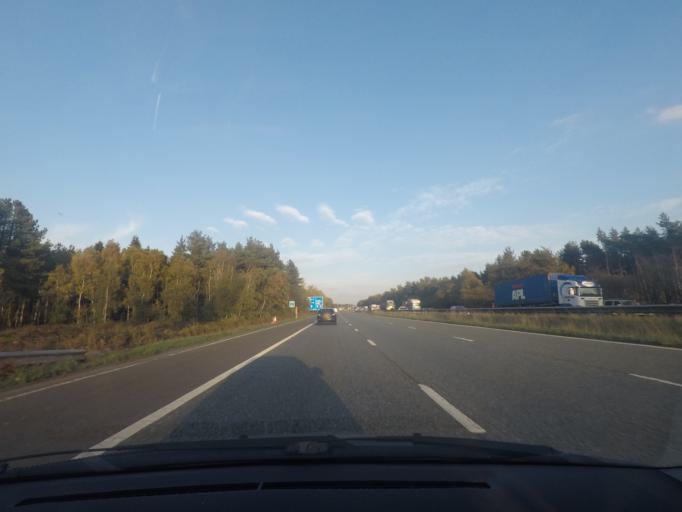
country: GB
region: England
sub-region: North Lincolnshire
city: Worlaby
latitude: 53.5798
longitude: -0.4477
